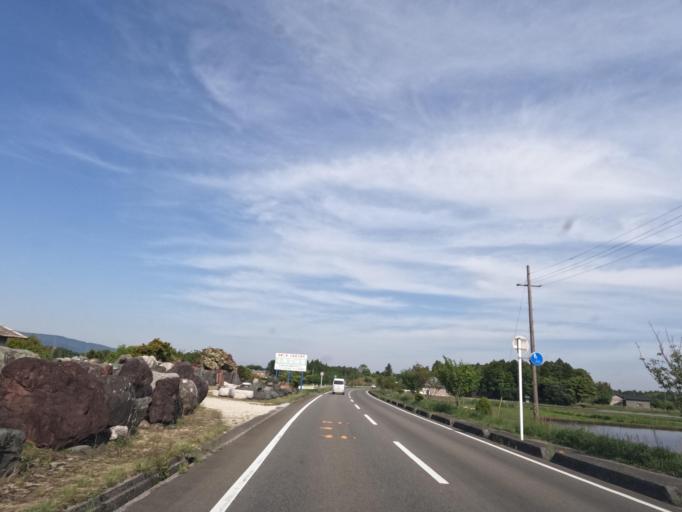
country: JP
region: Mie
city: Komono
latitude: 35.1103
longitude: 136.5127
